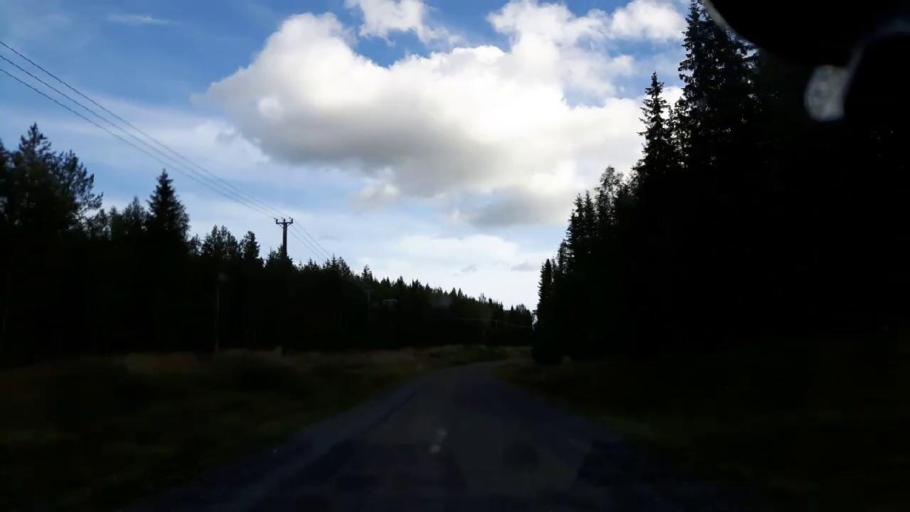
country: SE
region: Jaemtland
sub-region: Ragunda Kommun
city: Hammarstrand
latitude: 63.4185
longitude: 16.0746
